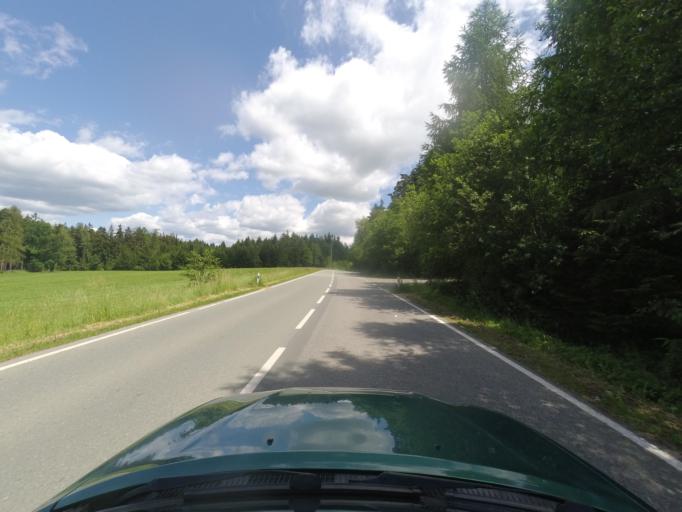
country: CZ
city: Vamberk
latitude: 50.1614
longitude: 16.3455
